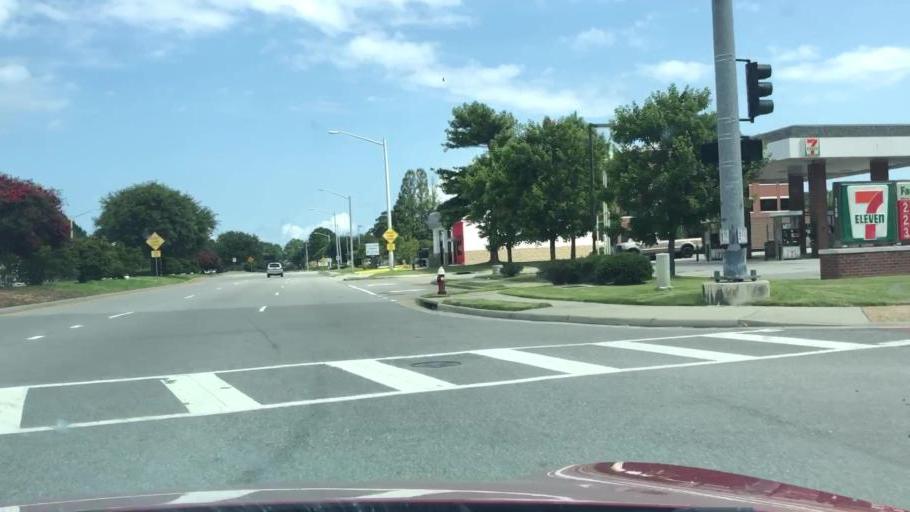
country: US
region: Virginia
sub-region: City of Chesapeake
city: Chesapeake
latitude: 36.8754
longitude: -76.1336
